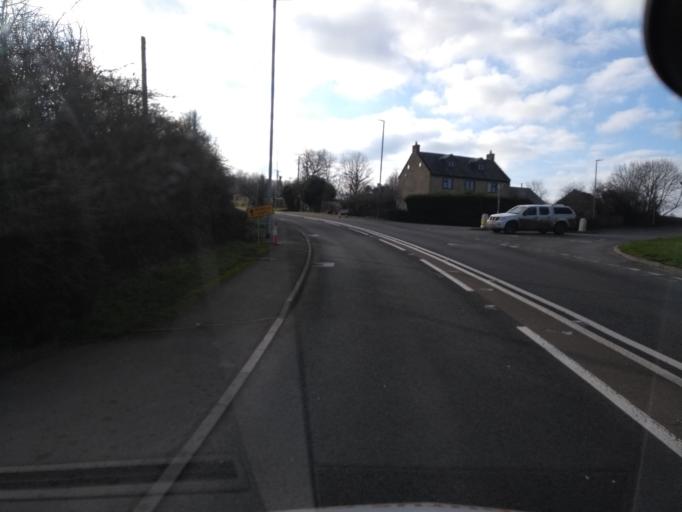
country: GB
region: England
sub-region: Somerset
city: Ilminster
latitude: 50.9326
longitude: -2.9462
